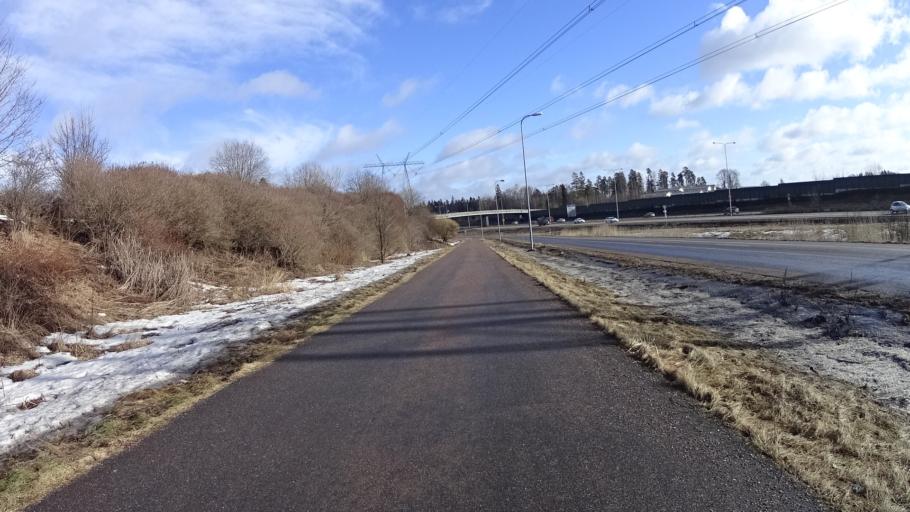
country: FI
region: Uusimaa
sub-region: Helsinki
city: Kauniainen
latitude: 60.2459
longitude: 24.7048
